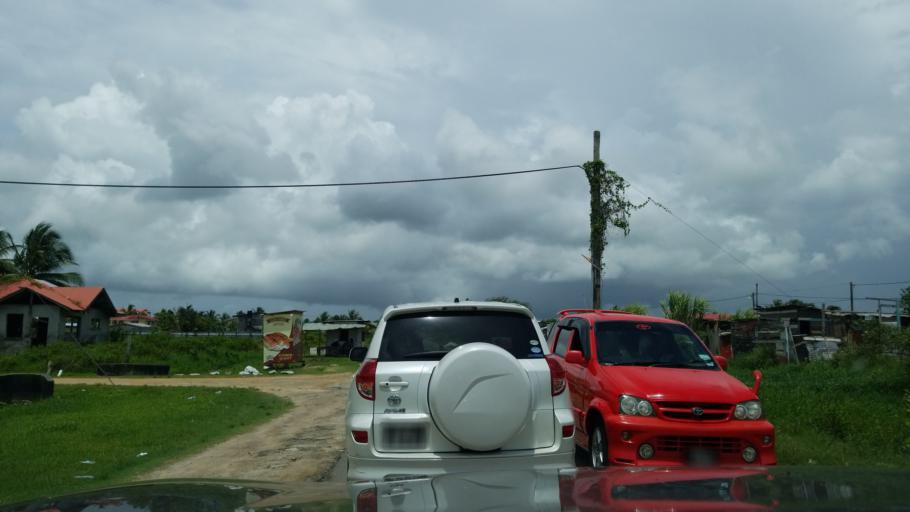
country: GY
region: Demerara-Mahaica
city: Georgetown
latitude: 6.8020
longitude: -58.1231
